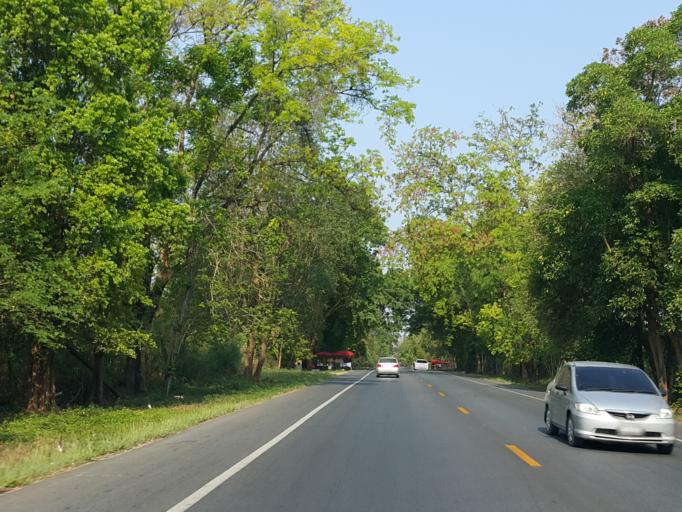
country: TH
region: Kanchanaburi
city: Sai Yok
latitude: 14.0899
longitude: 99.2982
